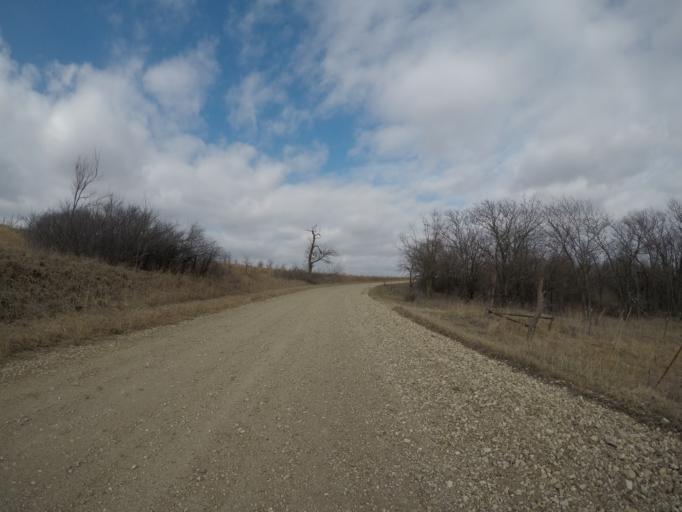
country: US
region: Kansas
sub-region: Morris County
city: Council Grove
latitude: 38.7753
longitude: -96.3528
